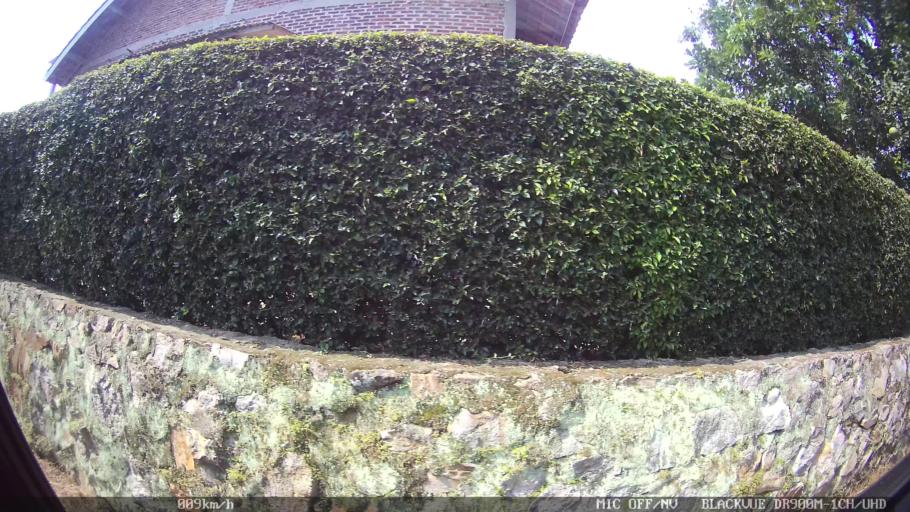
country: ID
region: Lampung
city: Kedaton
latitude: -5.3964
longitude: 105.2295
